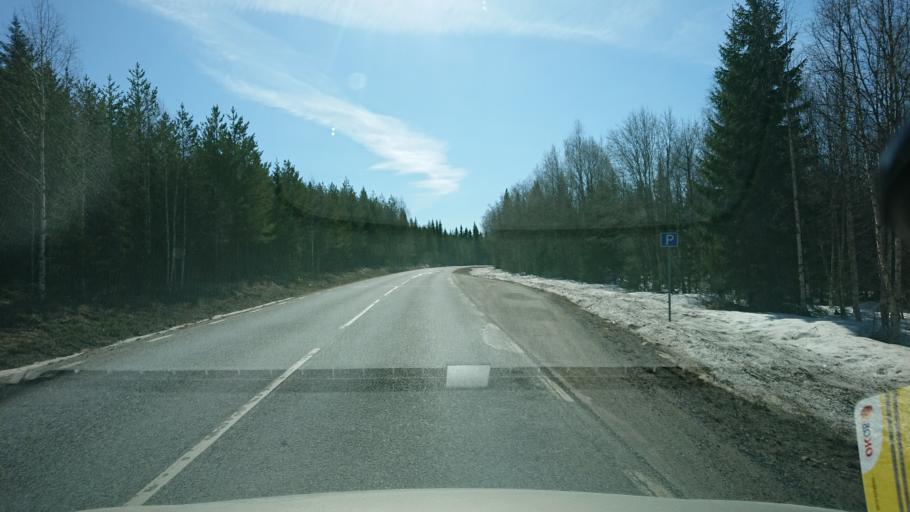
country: SE
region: Vaesterbotten
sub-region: Dorotea Kommun
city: Dorotea
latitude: 63.9926
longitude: 16.3159
